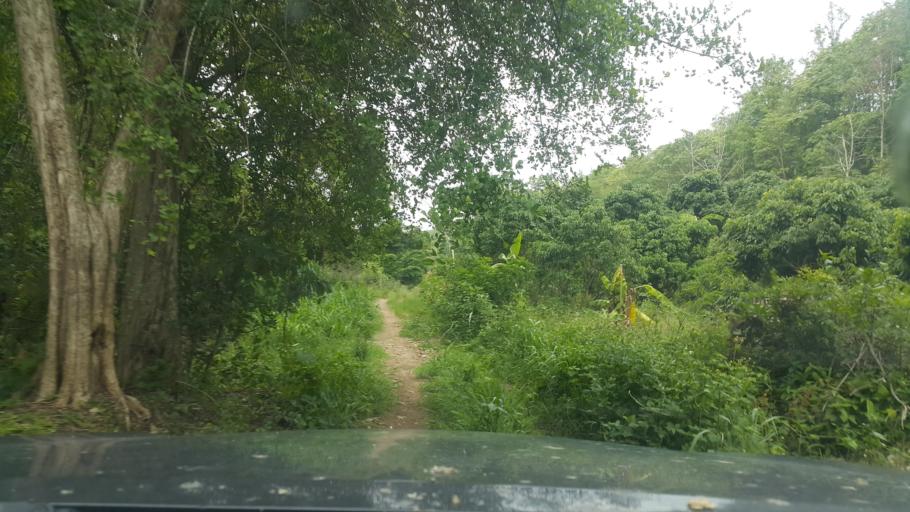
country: TH
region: Chiang Mai
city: Hang Dong
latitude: 18.6886
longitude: 98.8447
